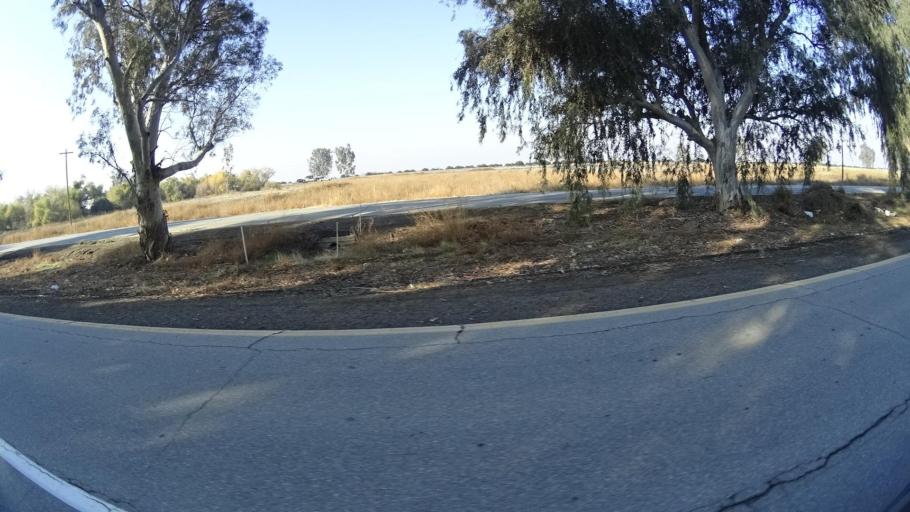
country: US
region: California
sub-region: Kern County
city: Greenfield
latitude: 35.1806
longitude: -119.0026
